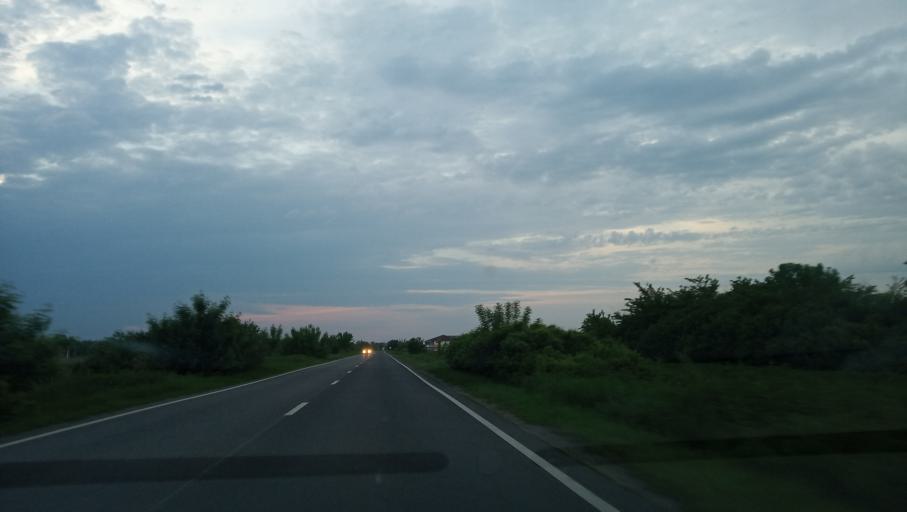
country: RO
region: Timis
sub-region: Comuna Jebel
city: Jebel
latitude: 45.5469
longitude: 21.2241
